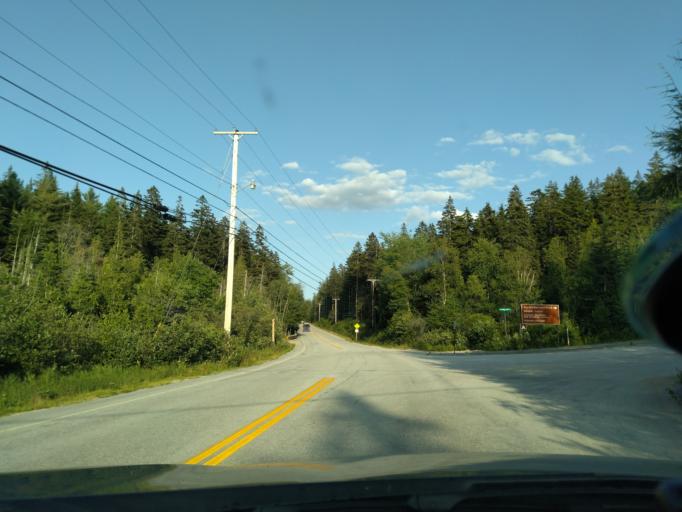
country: US
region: Maine
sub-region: Hancock County
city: Gouldsboro
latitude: 44.3940
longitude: -68.0741
